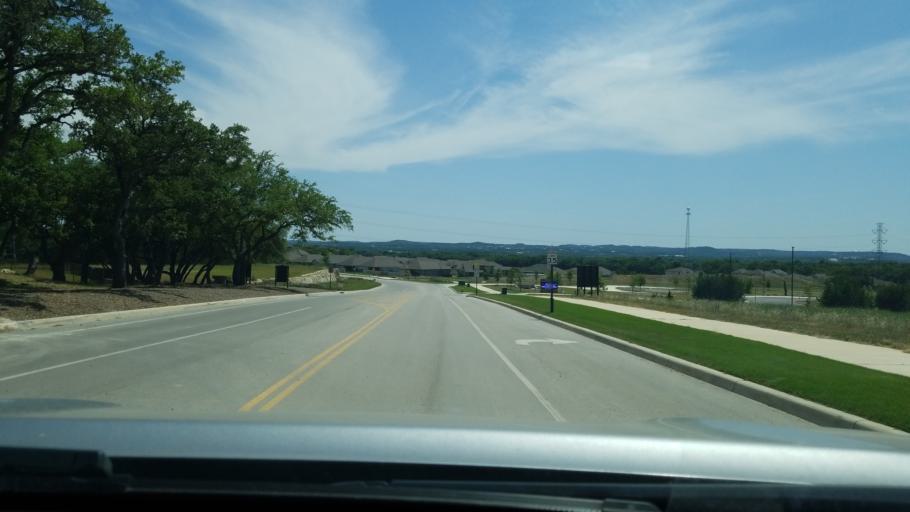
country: US
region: Texas
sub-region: Kendall County
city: Boerne
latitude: 29.8059
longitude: -98.6925
